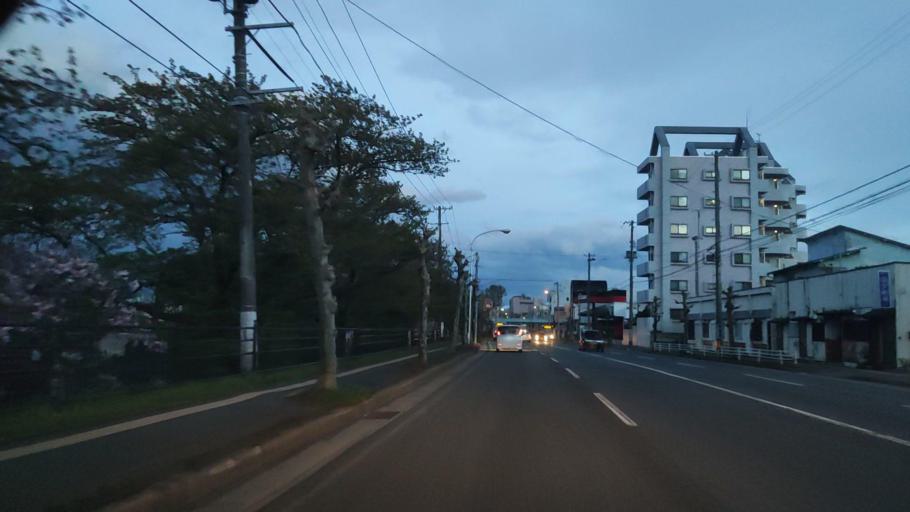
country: JP
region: Iwate
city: Morioka-shi
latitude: 39.7125
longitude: 141.1310
